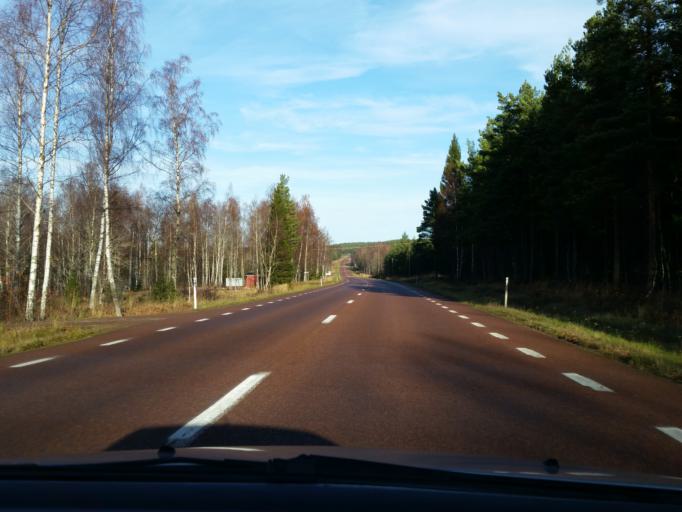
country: AX
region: Alands landsbygd
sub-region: Finstroem
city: Finstroem
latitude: 60.2928
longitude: 19.9534
